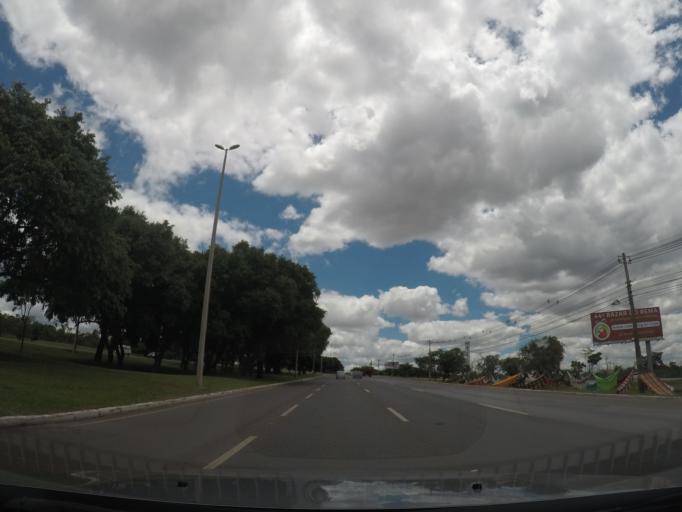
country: BR
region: Federal District
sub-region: Brasilia
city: Brasilia
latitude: -15.7532
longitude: -47.9253
